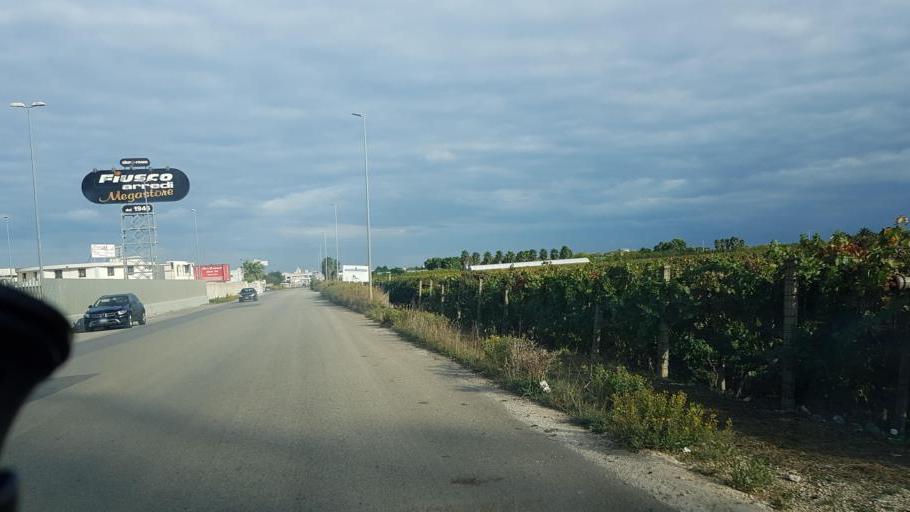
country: IT
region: Apulia
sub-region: Provincia di Brindisi
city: Francavilla Fontana
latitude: 40.5325
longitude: 17.5538
